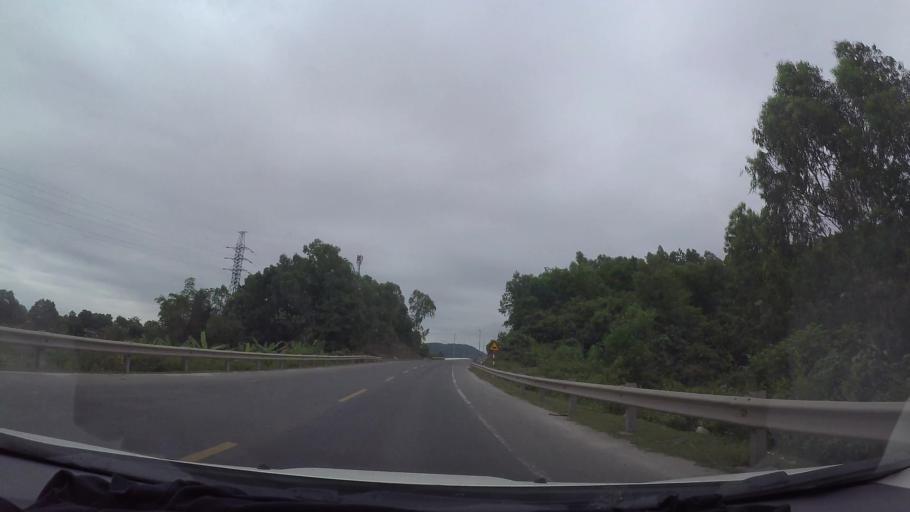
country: VN
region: Da Nang
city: Lien Chieu
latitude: 16.1175
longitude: 108.1040
